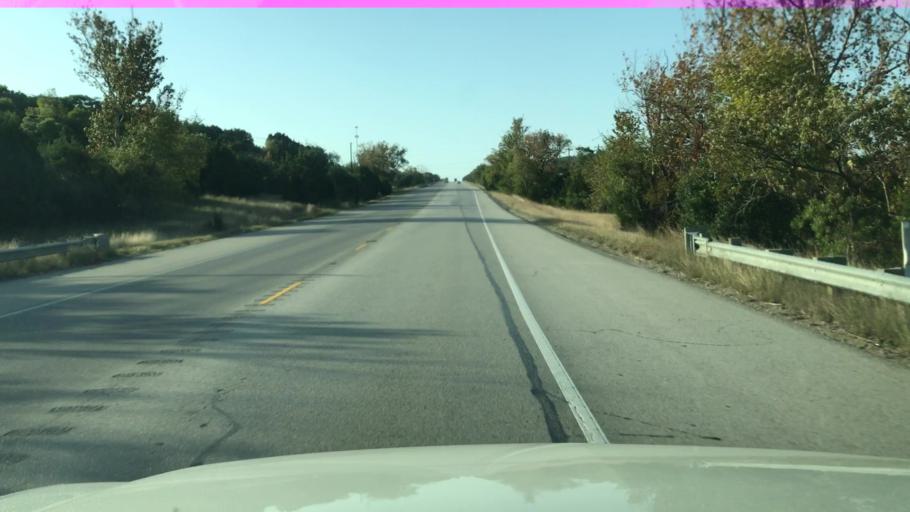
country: US
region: Texas
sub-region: Blanco County
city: Blanco
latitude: 30.1849
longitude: -98.3787
